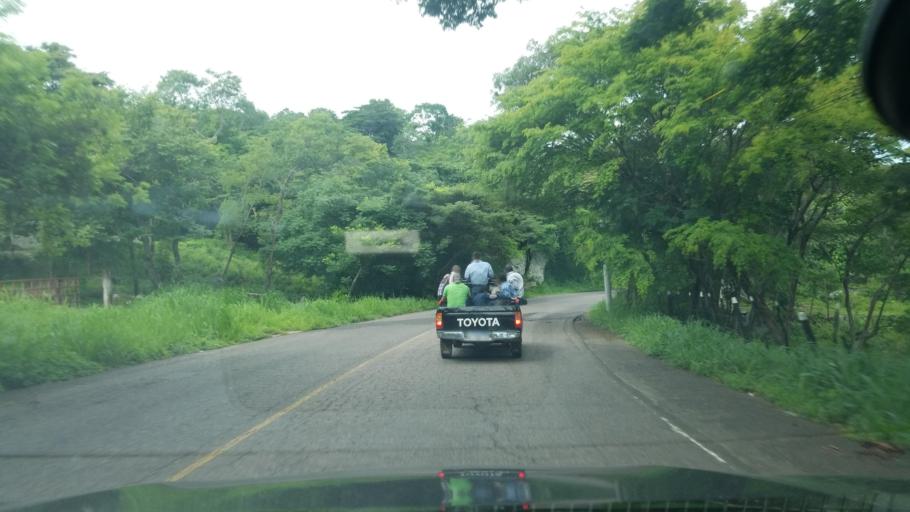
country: HN
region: Choluteca
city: Corpus
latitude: 13.3712
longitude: -87.0527
